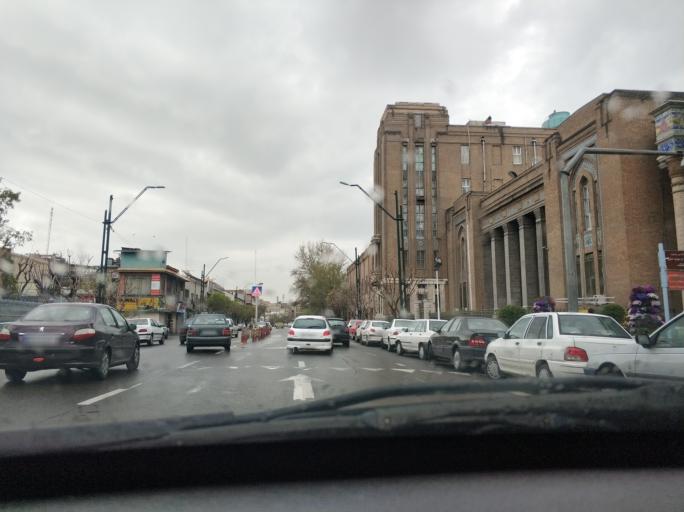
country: IR
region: Tehran
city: Tehran
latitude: 35.6859
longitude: 51.4171
